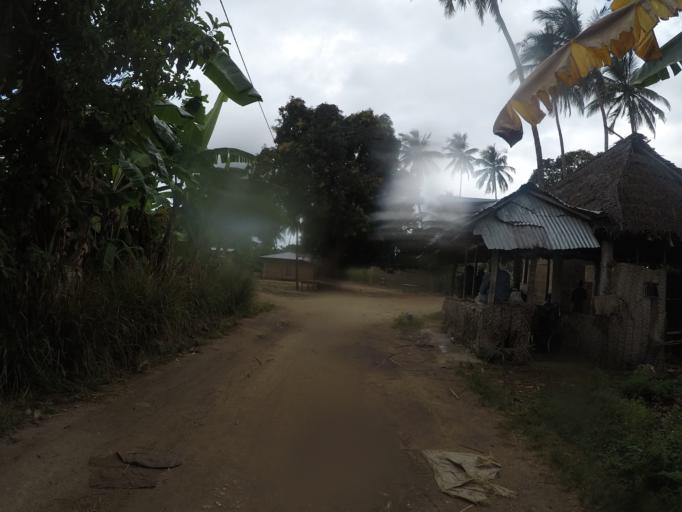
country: TZ
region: Zanzibar North
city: Mkokotoni
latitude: -5.9497
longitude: 39.1956
